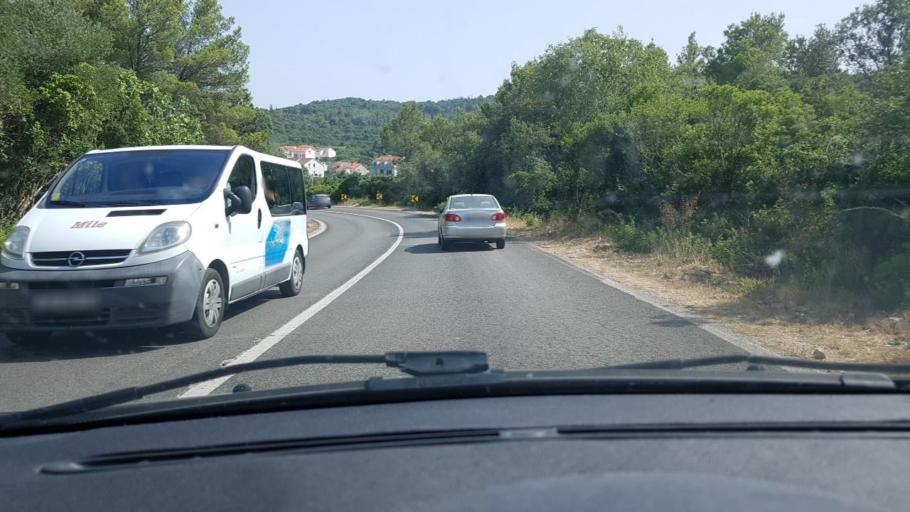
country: HR
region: Dubrovacko-Neretvanska
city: Korcula
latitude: 42.9497
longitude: 17.1314
